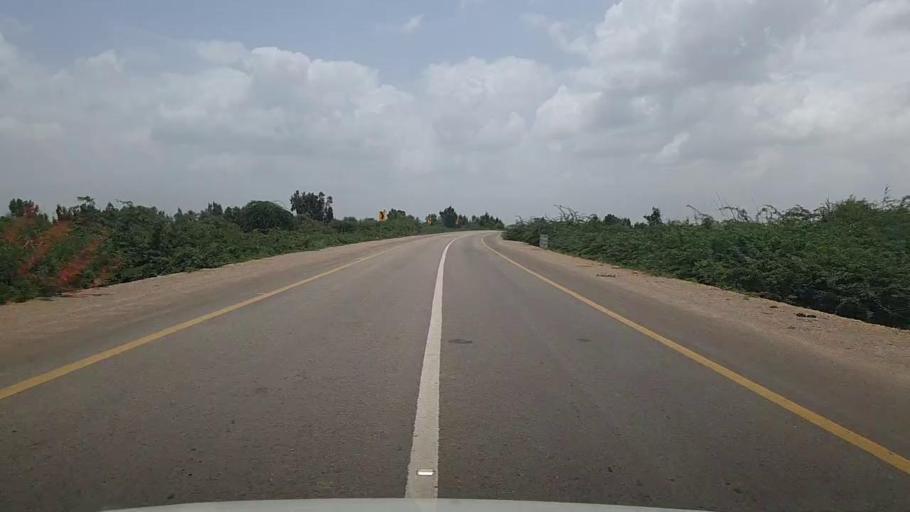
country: PK
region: Sindh
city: Thatta
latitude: 24.7423
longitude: 67.9492
